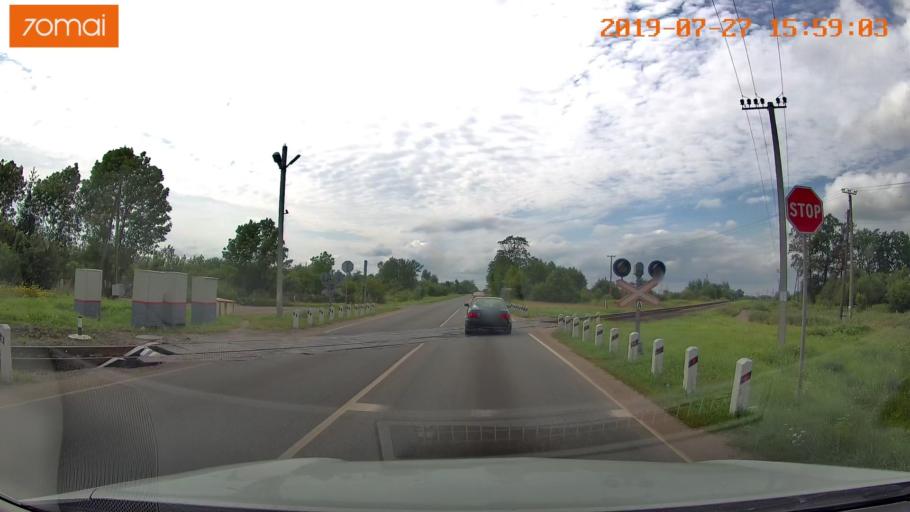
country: RU
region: Kaliningrad
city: Chernyakhovsk
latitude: 54.6265
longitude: 21.8572
